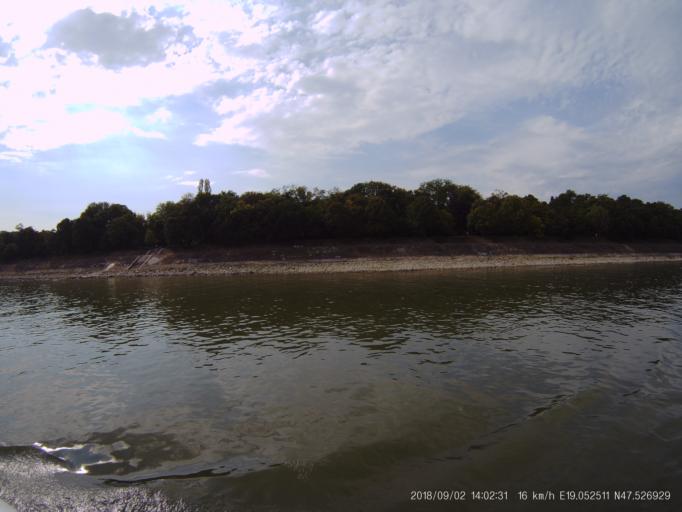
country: HU
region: Budapest
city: Budapest III. keruelet
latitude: 47.5269
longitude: 19.0525
